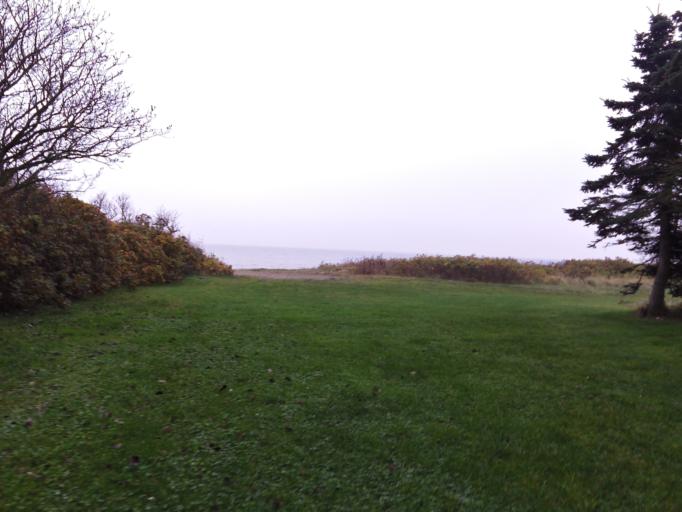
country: DK
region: Central Jutland
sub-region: Odder Kommune
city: Odder
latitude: 55.9314
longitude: 10.2574
